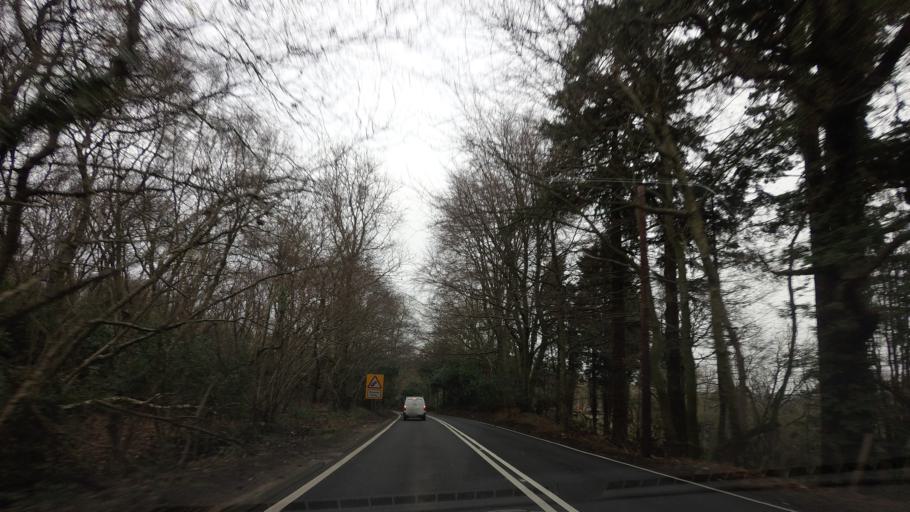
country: GB
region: England
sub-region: East Sussex
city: Saint Leonards-on-Sea
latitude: 50.8956
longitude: 0.5562
